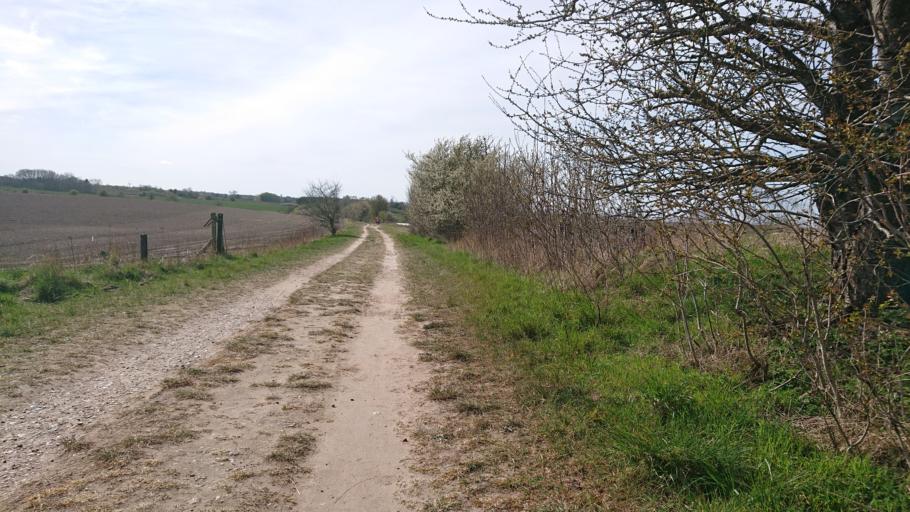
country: DK
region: South Denmark
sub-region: Nyborg Kommune
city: Nyborg
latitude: 55.3005
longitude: 10.7475
